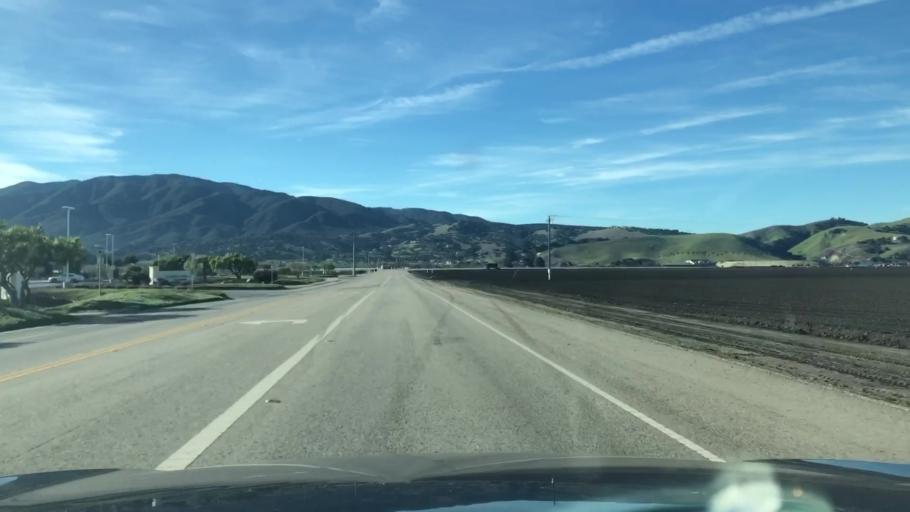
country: US
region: California
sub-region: Monterey County
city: Salinas
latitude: 36.6232
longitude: -121.6315
